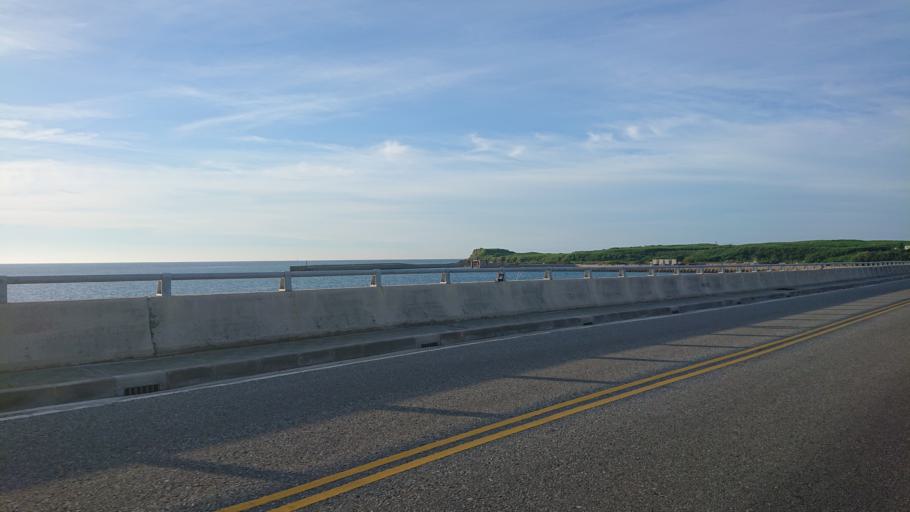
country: TW
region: Taiwan
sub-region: Penghu
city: Ma-kung
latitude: 23.6545
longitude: 119.5516
